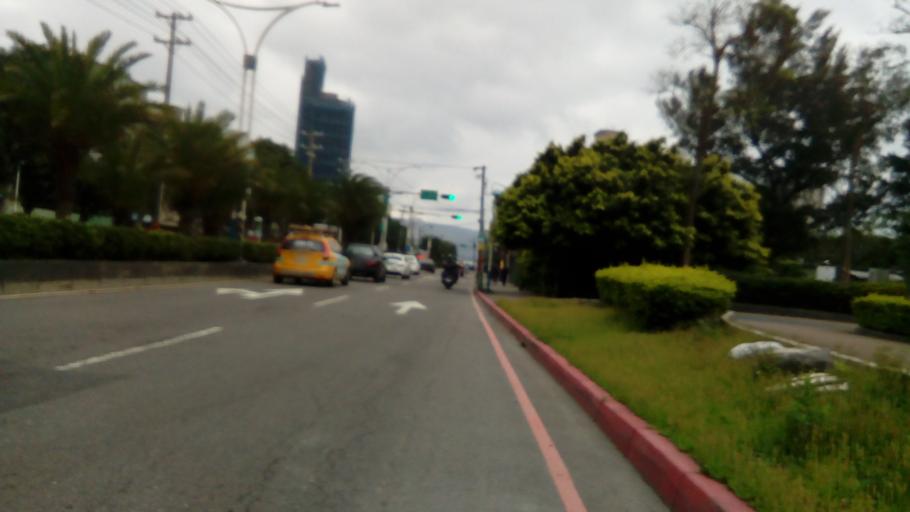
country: TW
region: Taipei
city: Taipei
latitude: 25.1773
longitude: 121.4246
